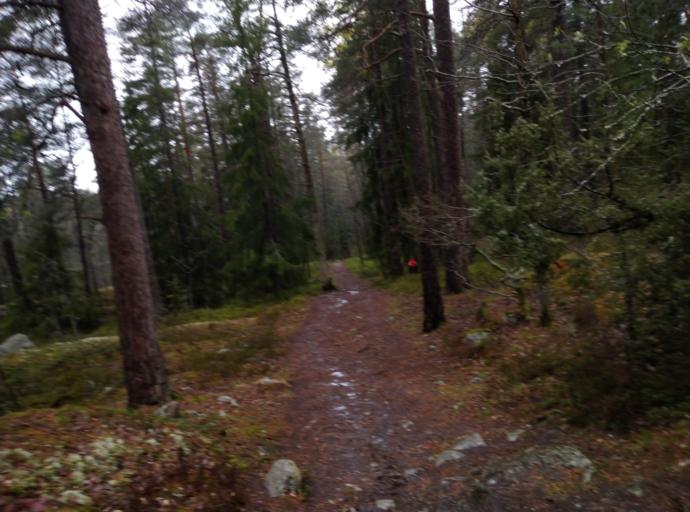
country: SE
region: Stockholm
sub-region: Nacka Kommun
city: Fisksatra
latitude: 59.2935
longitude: 18.2708
